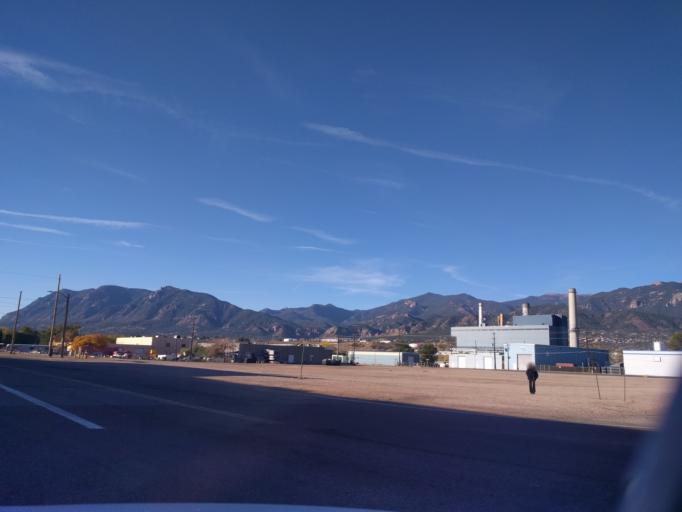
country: US
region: Colorado
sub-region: El Paso County
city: Colorado Springs
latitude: 38.8269
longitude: -104.8275
